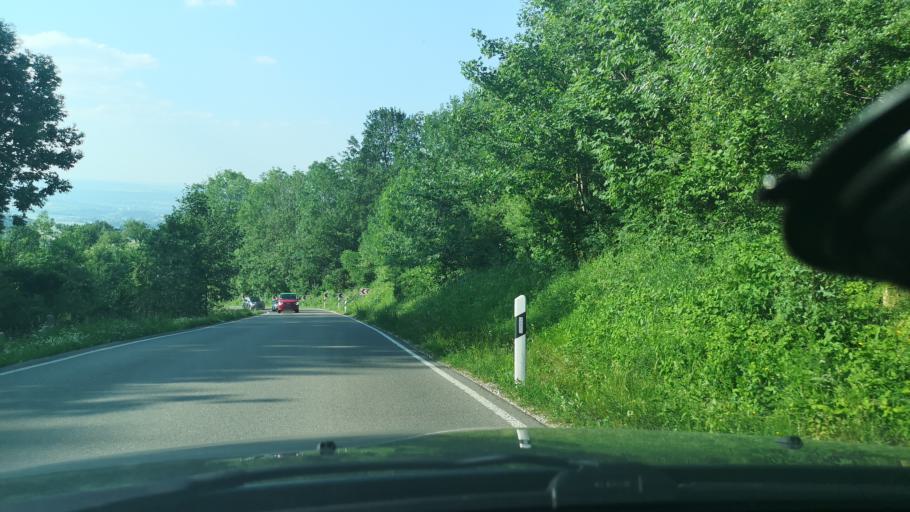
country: DE
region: Baden-Wuerttemberg
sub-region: Regierungsbezirk Stuttgart
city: Schlat
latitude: 48.6367
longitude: 9.7039
